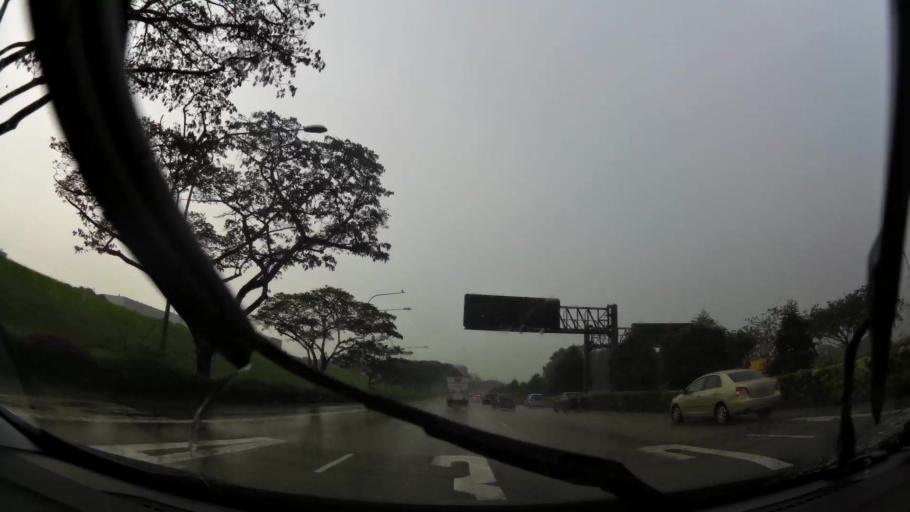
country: MY
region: Johor
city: Kampung Pasir Gudang Baru
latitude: 1.3779
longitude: 103.9254
